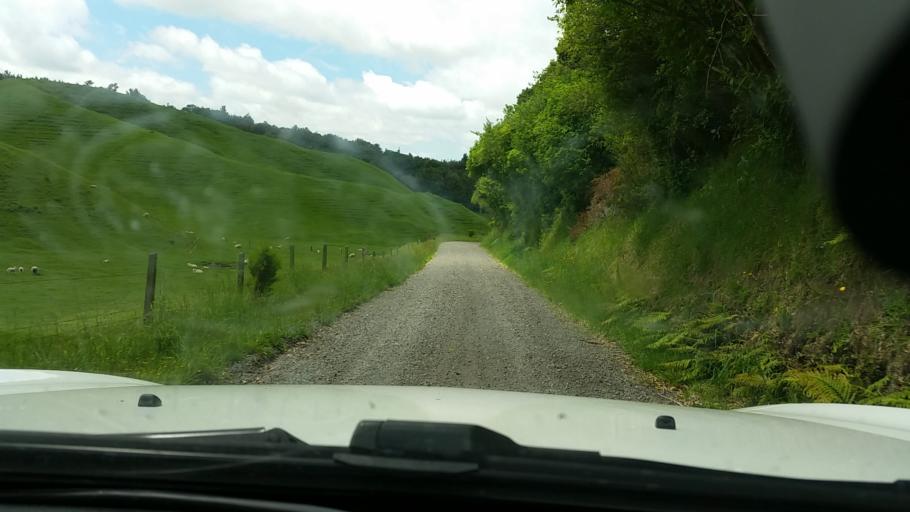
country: NZ
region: Bay of Plenty
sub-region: Rotorua District
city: Rotorua
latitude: -37.9832
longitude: 176.3986
